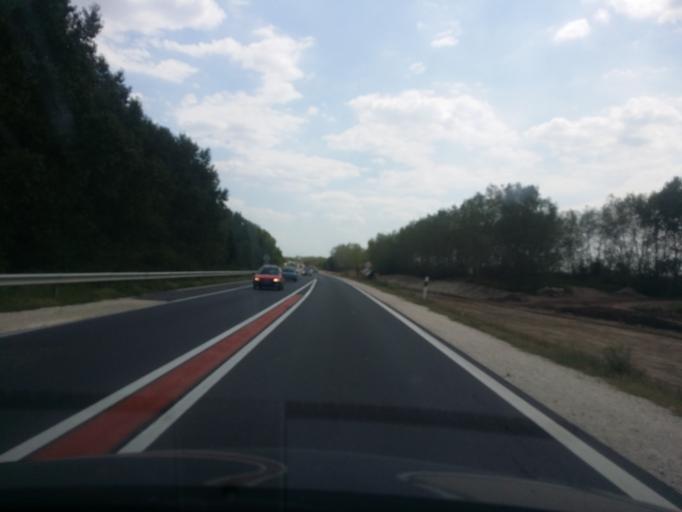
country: HU
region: Pest
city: Dunakeszi
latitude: 47.6460
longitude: 19.1622
